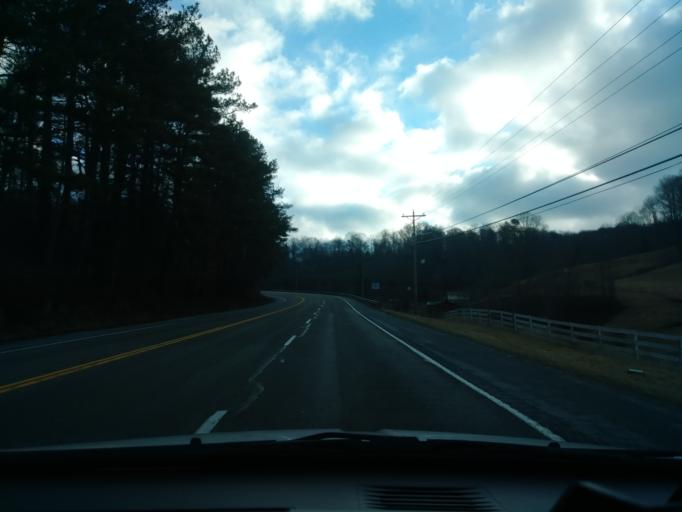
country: US
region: Tennessee
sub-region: Carter County
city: Roan Mountain
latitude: 36.2266
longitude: -82.1706
